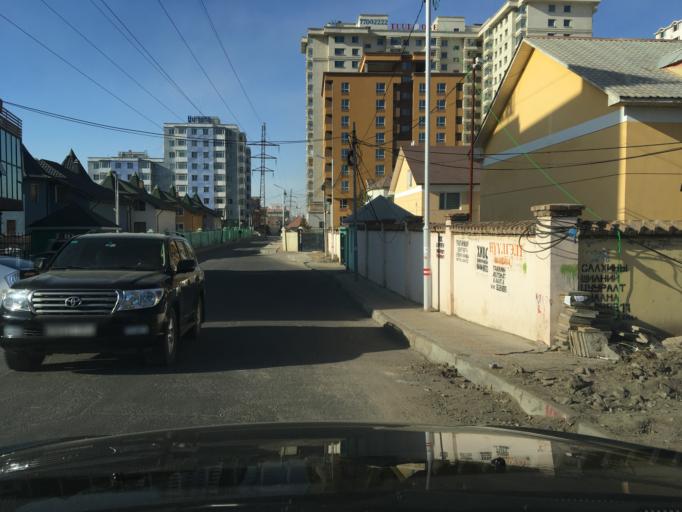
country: MN
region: Ulaanbaatar
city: Ulaanbaatar
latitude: 47.8926
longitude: 106.9087
